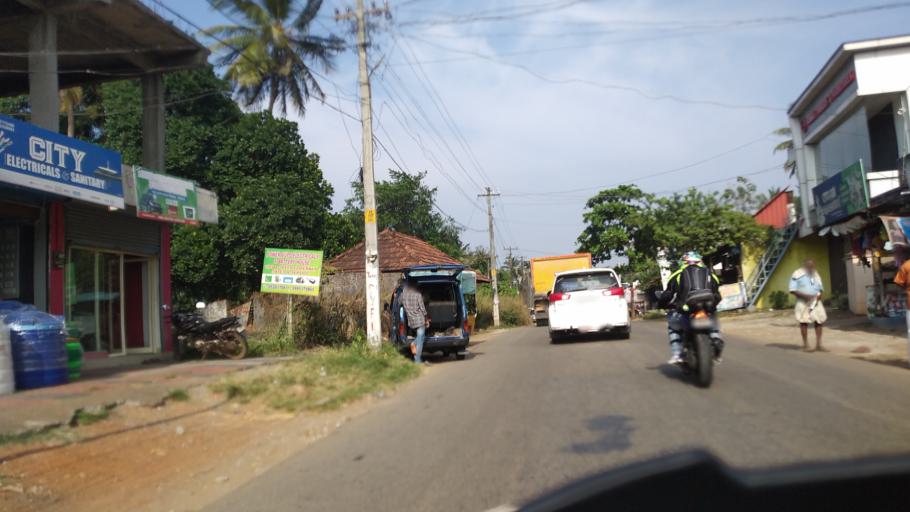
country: IN
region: Kerala
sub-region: Thrissur District
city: Chelakara
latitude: 10.5910
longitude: 76.5179
